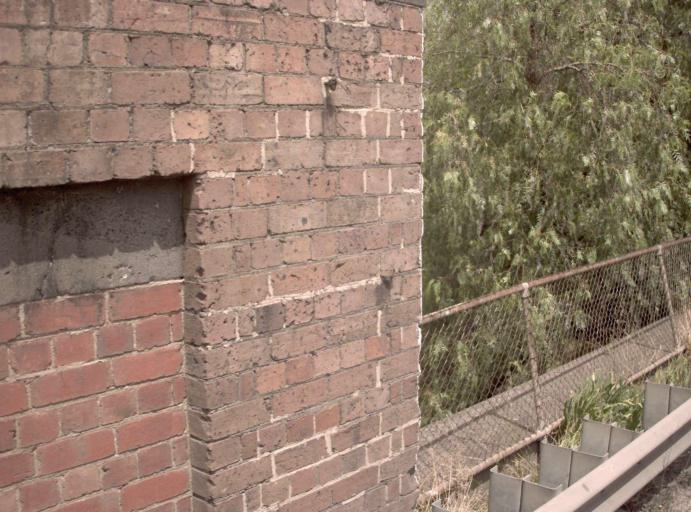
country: AU
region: Victoria
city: Alphington
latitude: -37.7875
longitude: 145.0255
